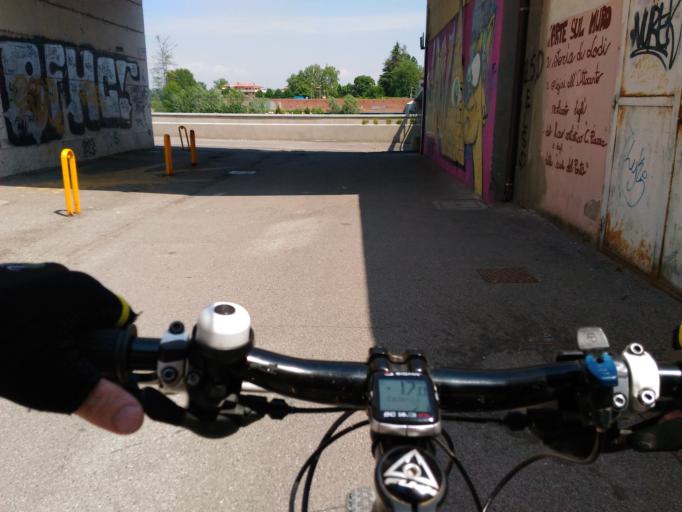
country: IT
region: Lombardy
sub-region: Provincia di Lodi
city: Lodi
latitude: 45.3183
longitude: 9.5075
